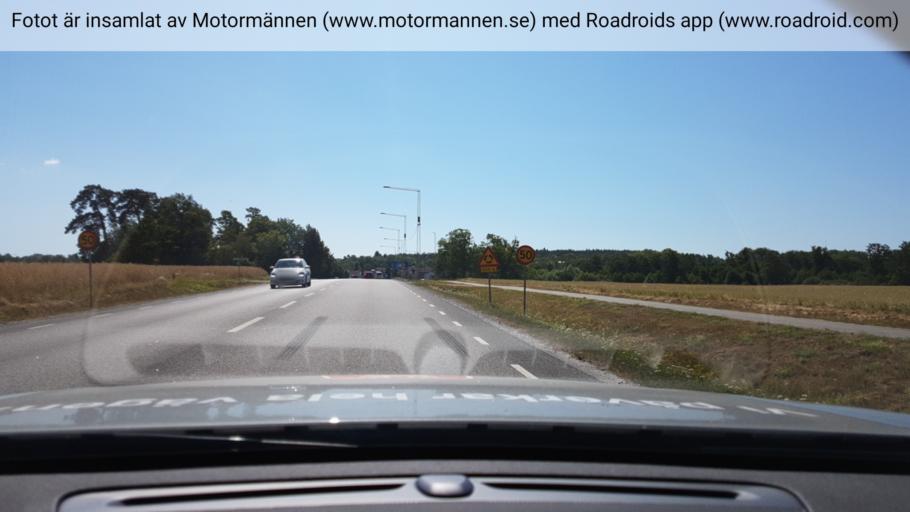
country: SE
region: Stockholm
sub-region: Ekero Kommun
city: Ekeroe
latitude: 59.2961
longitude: 17.8111
